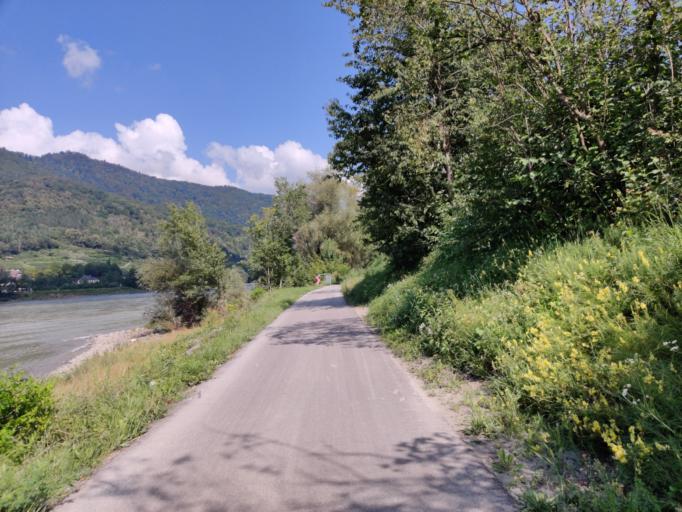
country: AT
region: Lower Austria
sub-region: Politischer Bezirk Krems
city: Spitz
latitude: 48.3371
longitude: 15.4092
